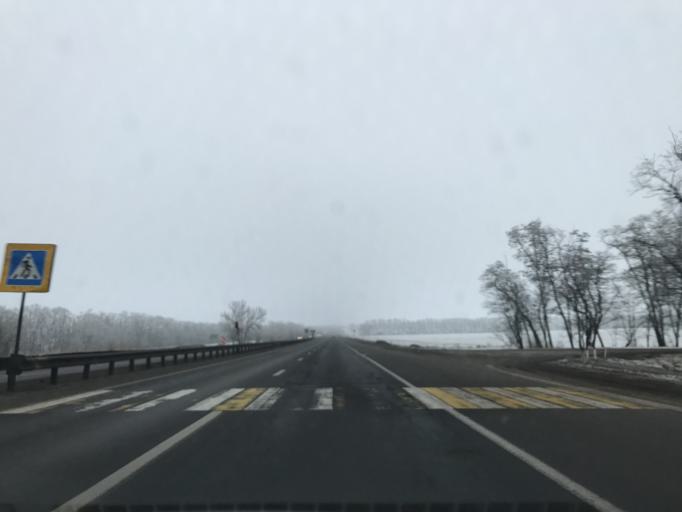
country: RU
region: Rostov
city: Grushevskaya
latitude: 47.4726
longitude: 39.9721
